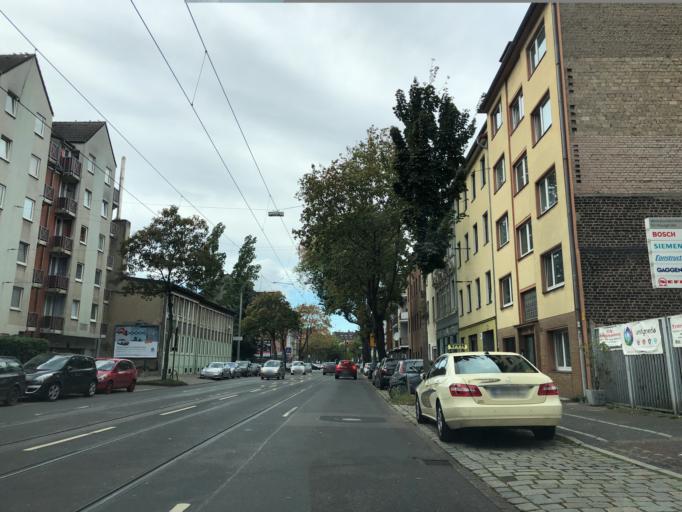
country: DE
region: North Rhine-Westphalia
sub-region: Regierungsbezirk Dusseldorf
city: Dusseldorf
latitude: 51.2094
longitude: 6.8052
